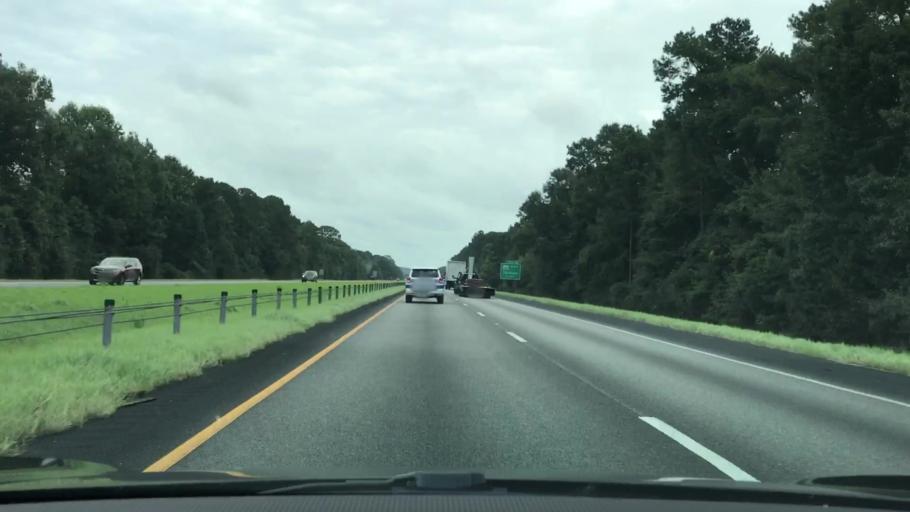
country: US
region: Alabama
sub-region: Elmore County
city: Tallassee
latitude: 32.4252
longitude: -85.9207
